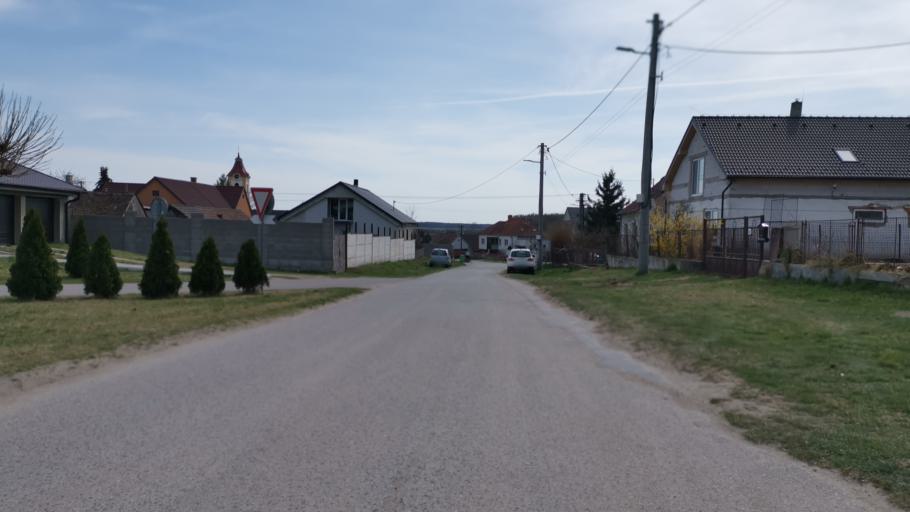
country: SK
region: Trnavsky
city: Gbely
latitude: 48.6574
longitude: 17.0959
